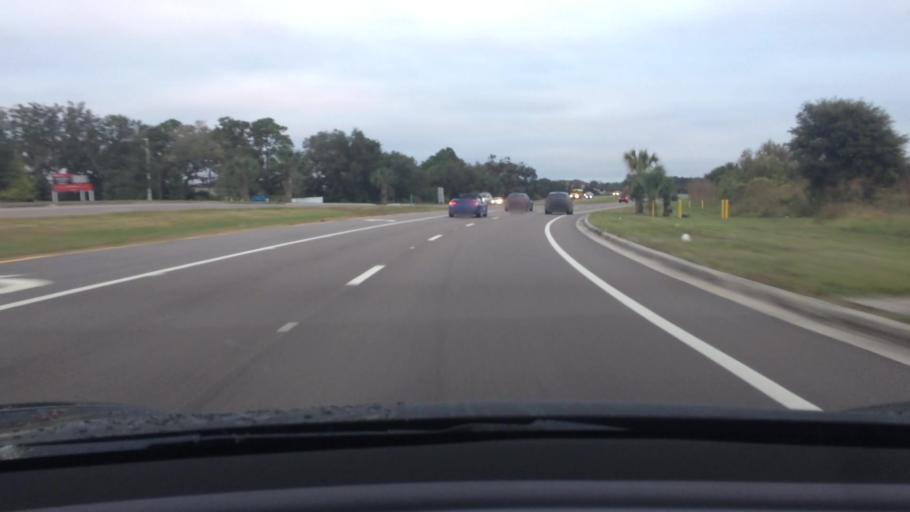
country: US
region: Florida
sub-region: Hillsborough County
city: Progress Village
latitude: 27.8878
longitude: -82.3587
